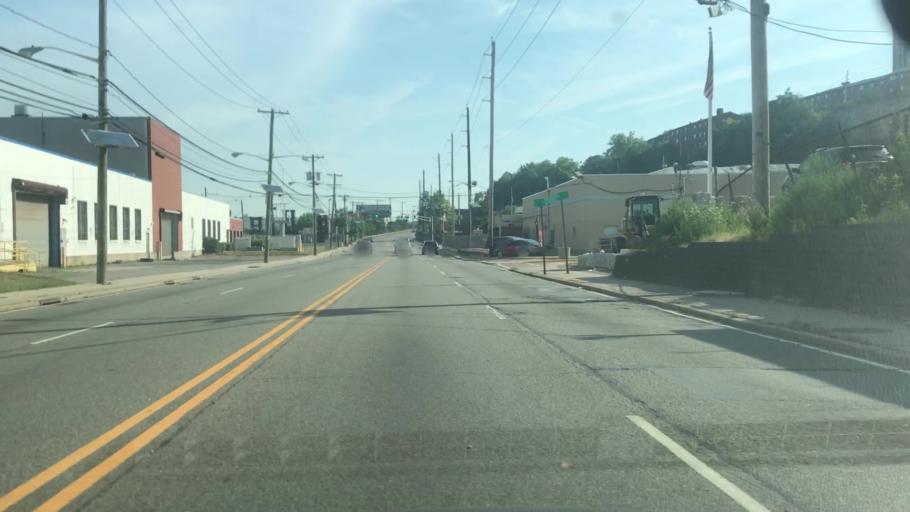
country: US
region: New Jersey
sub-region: Hudson County
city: West New York
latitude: 40.7943
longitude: -74.0267
